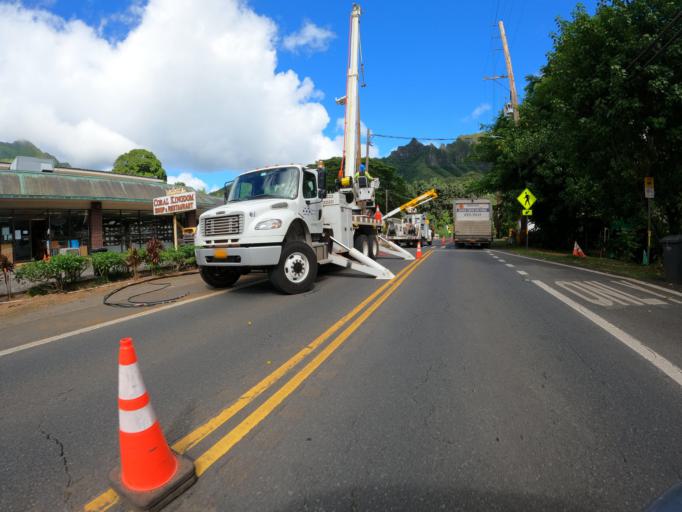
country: US
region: Hawaii
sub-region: Honolulu County
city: Ka'a'awa
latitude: 21.5064
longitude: -157.8550
